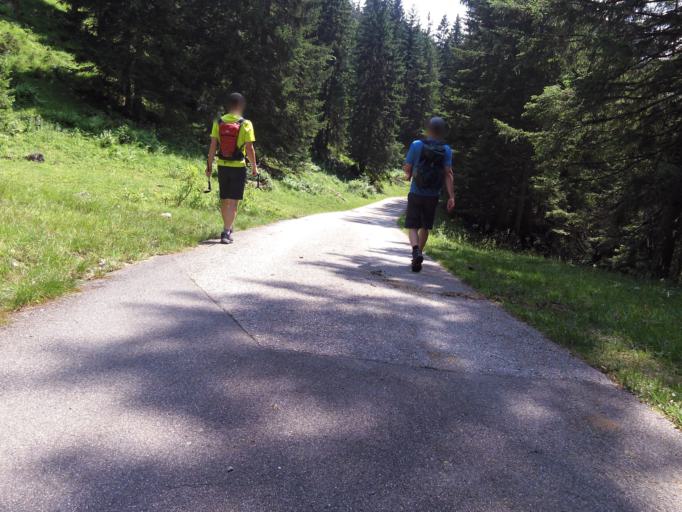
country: AT
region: Tyrol
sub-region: Politischer Bezirk Kitzbuhel
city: Waidring
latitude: 47.6652
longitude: 12.5900
